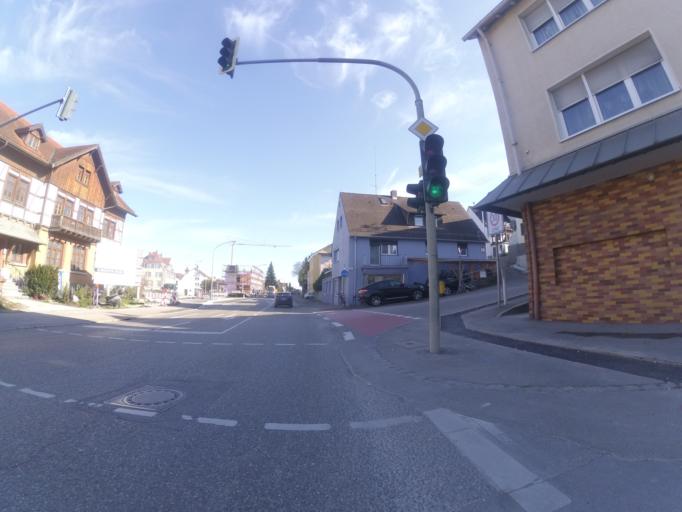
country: DE
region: Baden-Wuerttemberg
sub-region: Tuebingen Region
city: Dornstadt
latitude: 48.4184
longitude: 9.9083
